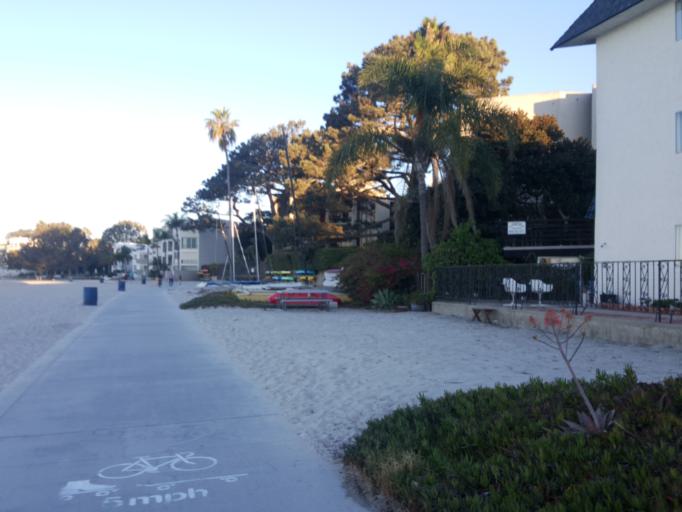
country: US
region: California
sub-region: San Diego County
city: La Jolla
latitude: 32.7903
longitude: -117.2422
